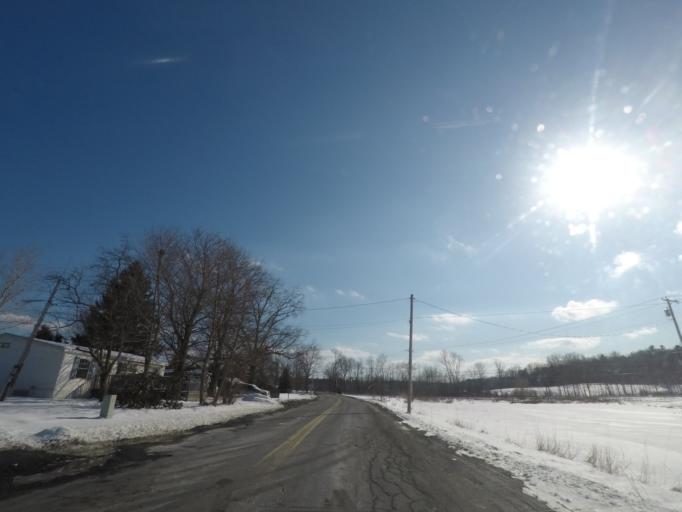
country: US
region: New York
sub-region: Rensselaer County
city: Hoosick Falls
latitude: 42.8998
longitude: -73.5013
